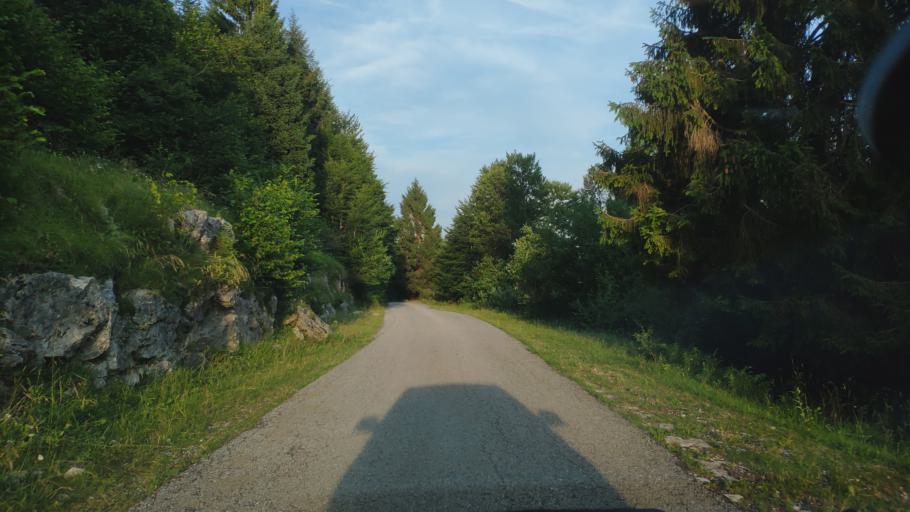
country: IT
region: Veneto
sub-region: Provincia di Vicenza
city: Calvene
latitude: 45.7983
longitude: 11.4967
